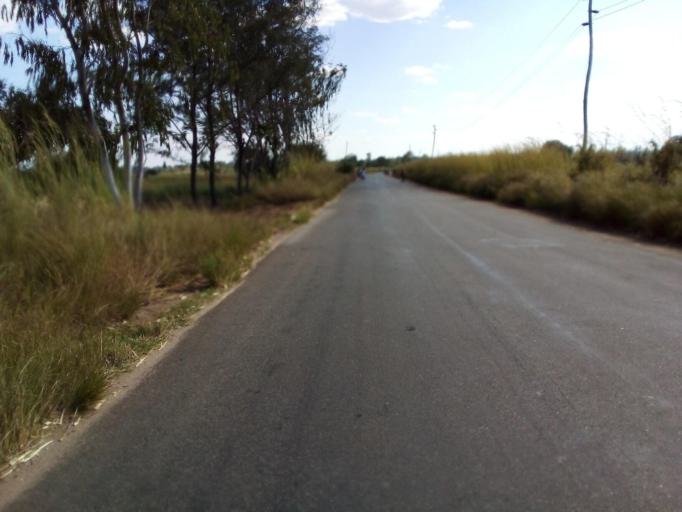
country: MZ
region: Zambezia
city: Quelimane
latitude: -17.5778
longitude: 36.6843
